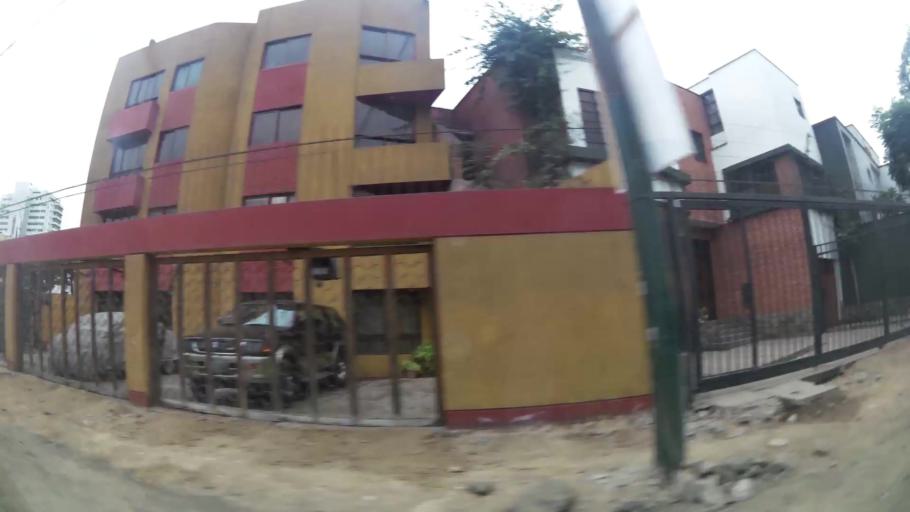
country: PE
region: Lima
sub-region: Lima
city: San Isidro
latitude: -12.0944
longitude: -77.0311
